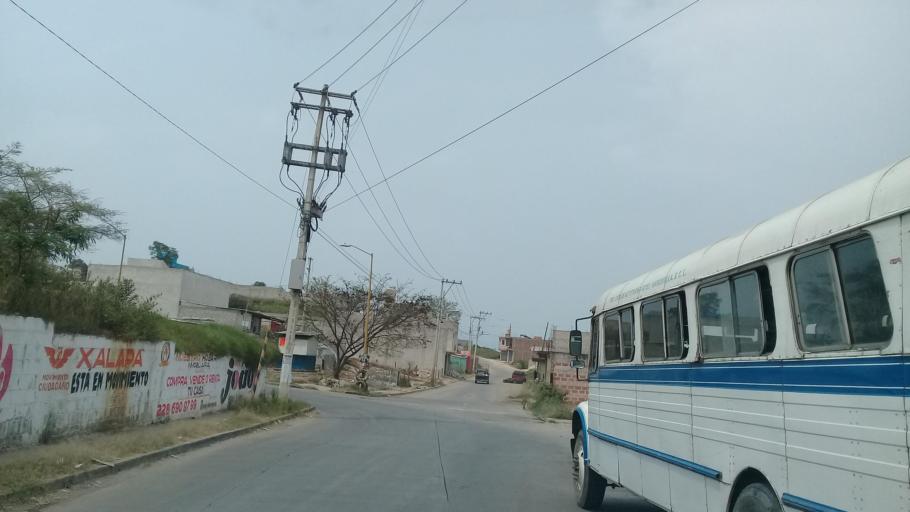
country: MX
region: Veracruz
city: El Castillo
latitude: 19.5600
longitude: -96.8872
